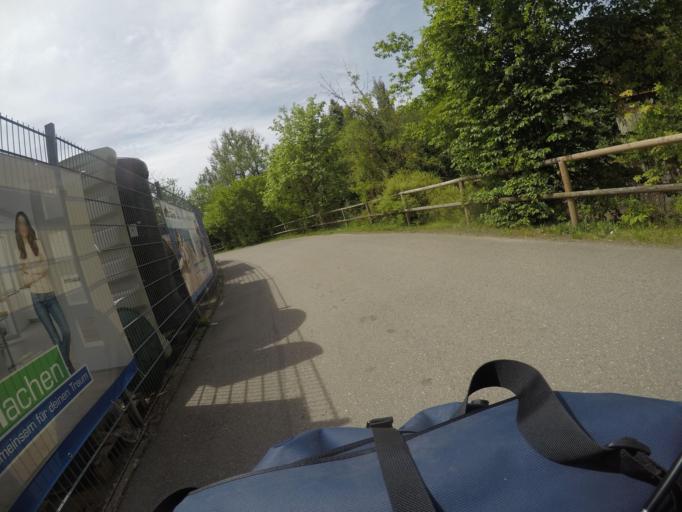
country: DE
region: Baden-Wuerttemberg
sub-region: Karlsruhe Region
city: Nagold
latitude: 48.5620
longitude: 8.7242
